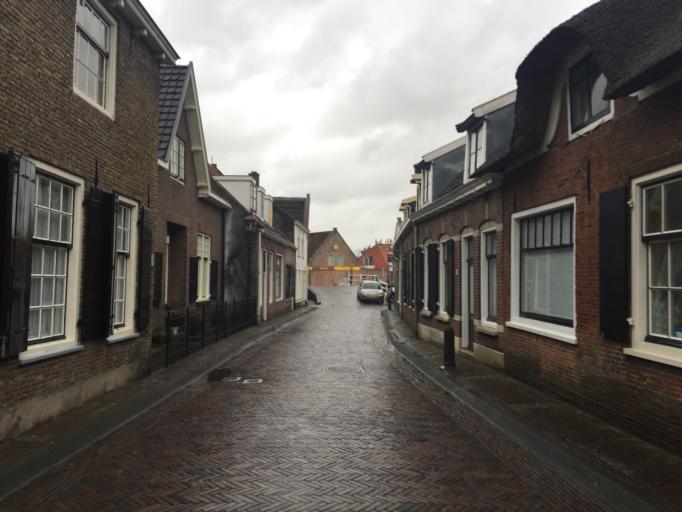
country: NL
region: Utrecht
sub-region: Gemeente Woerden
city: Woerden
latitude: 52.0614
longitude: 4.9152
